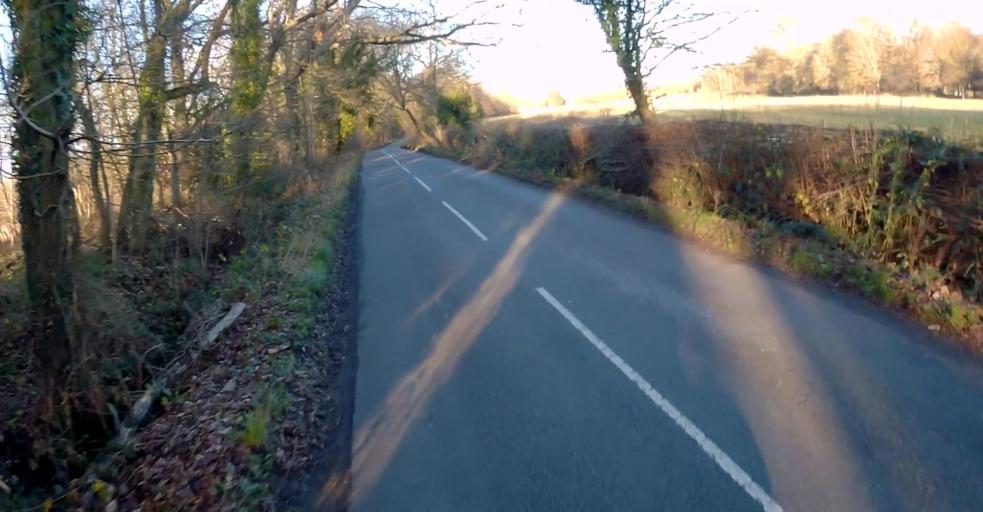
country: GB
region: England
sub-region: Hampshire
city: Hook
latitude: 51.2856
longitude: -0.9820
